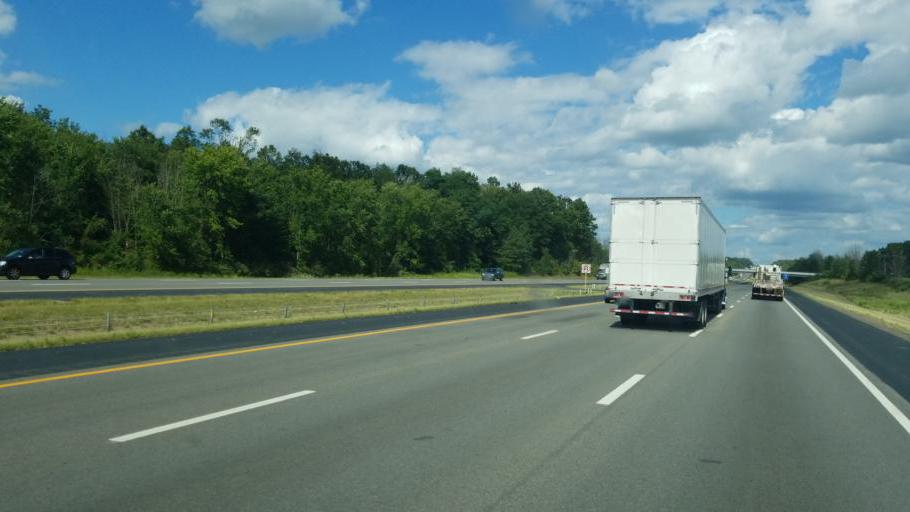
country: US
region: Ohio
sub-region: Medina County
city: Westfield Center
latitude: 41.0093
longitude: -81.9450
